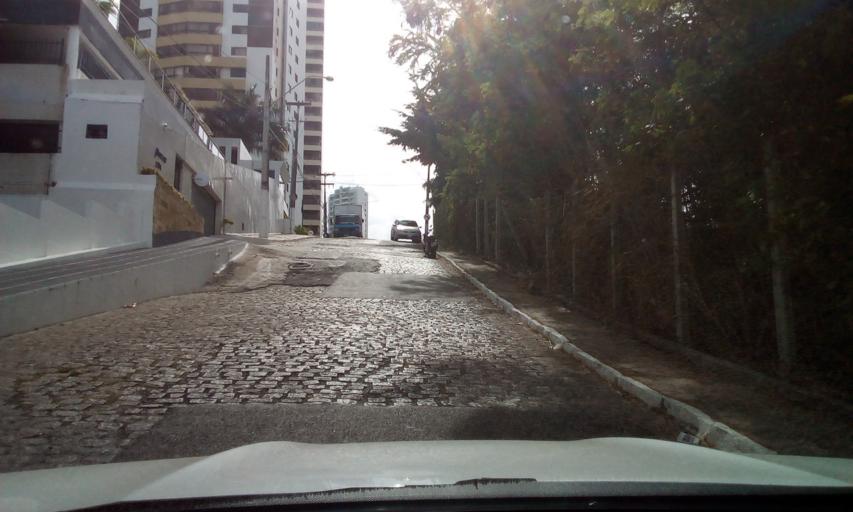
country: BR
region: Paraiba
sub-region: Joao Pessoa
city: Joao Pessoa
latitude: -7.1208
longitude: -34.8318
